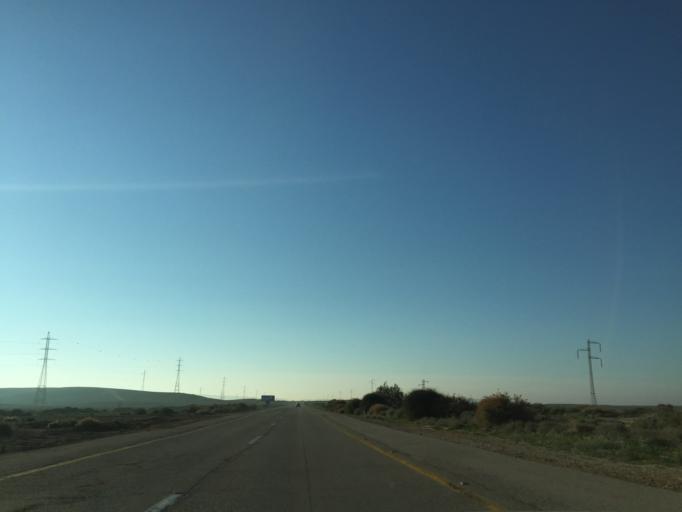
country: IL
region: Southern District
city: Mitzpe Ramon
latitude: 30.4571
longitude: 34.9355
